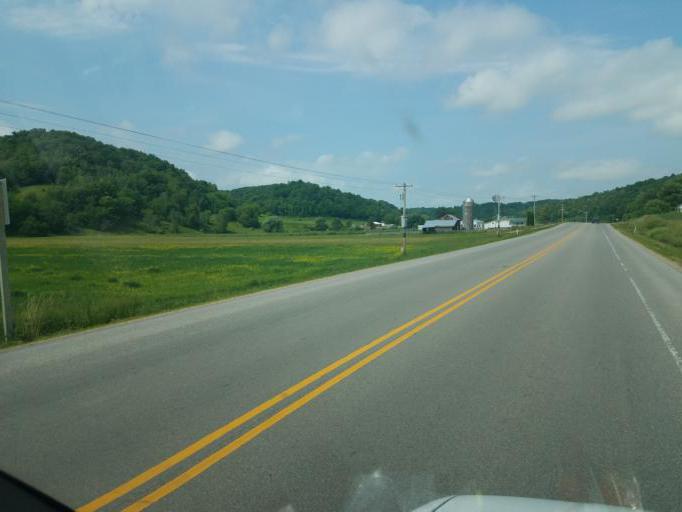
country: US
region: Wisconsin
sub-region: Monroe County
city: Cashton
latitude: 43.7337
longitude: -90.6906
